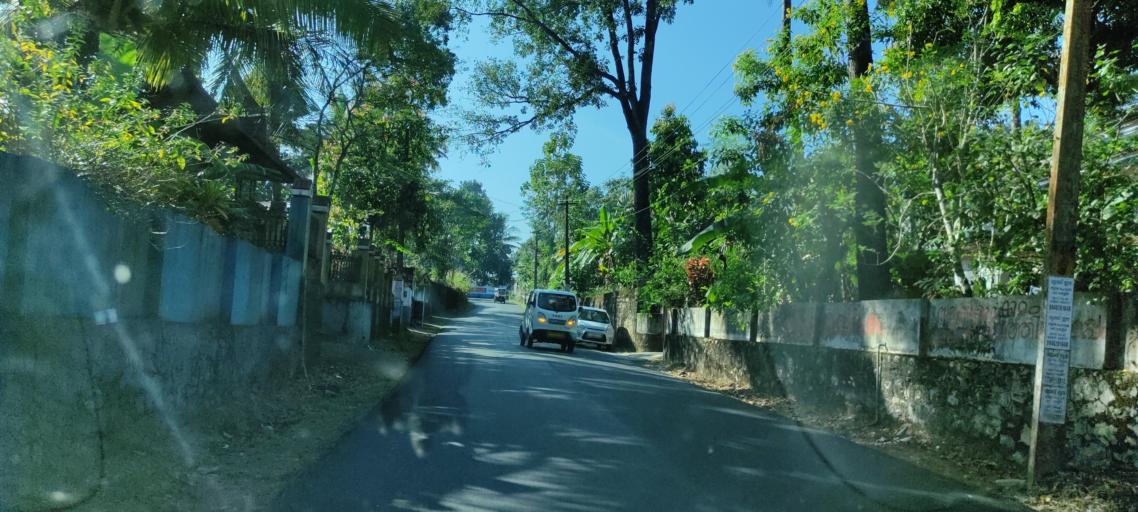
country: IN
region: Kerala
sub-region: Pattanamtitta
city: Adur
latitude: 9.1598
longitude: 76.7147
